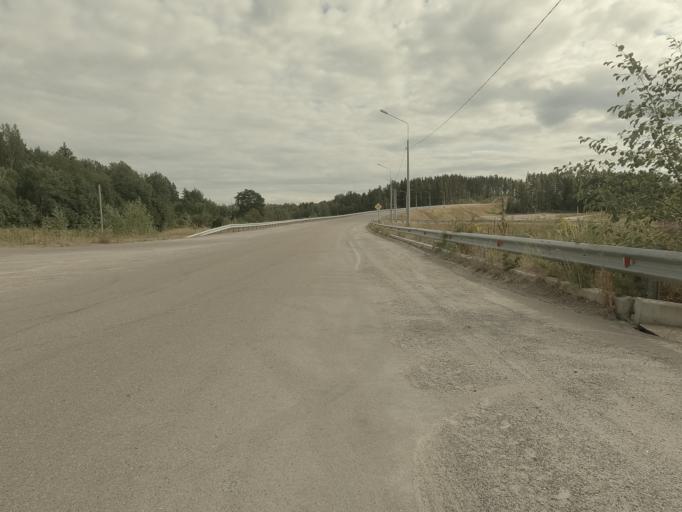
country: RU
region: Leningrad
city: Kamennogorsk
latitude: 60.9653
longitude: 29.1406
